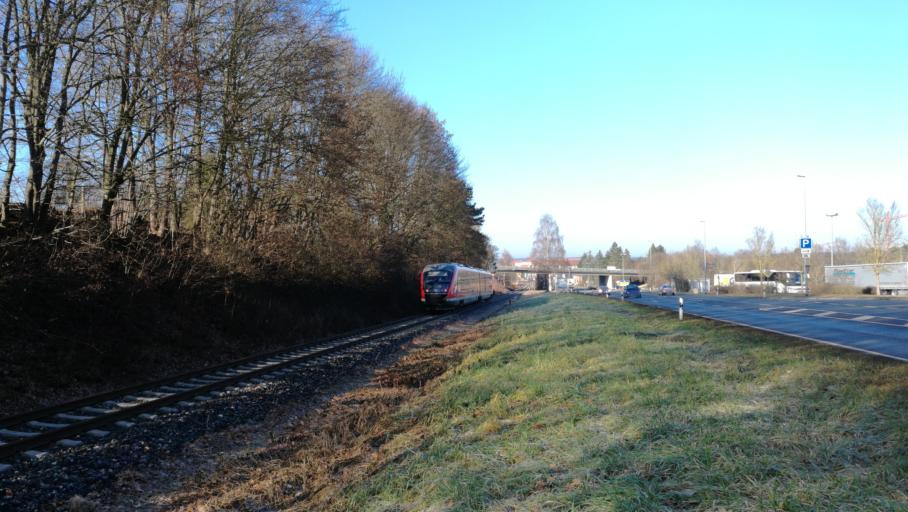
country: DE
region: Bavaria
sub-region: Regierungsbezirk Mittelfranken
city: Roth
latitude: 49.2392
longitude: 11.1073
